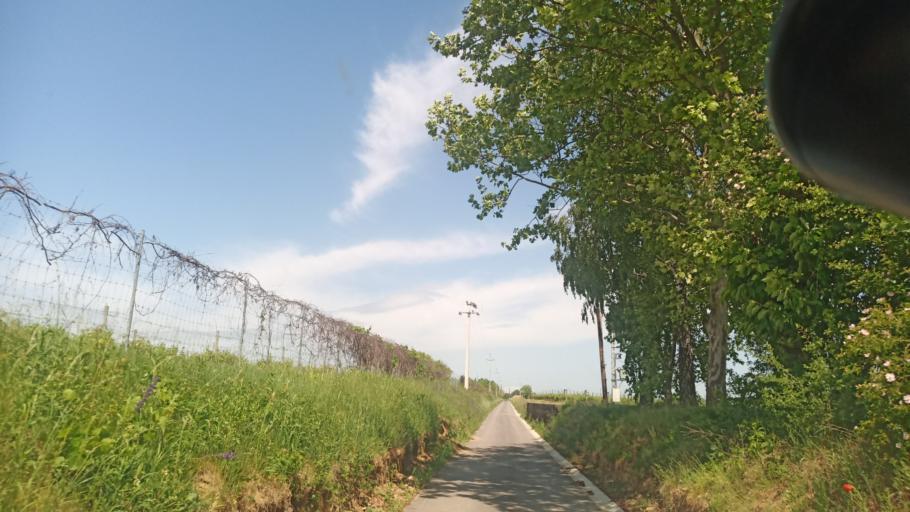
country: HU
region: Zala
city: Zalakomar
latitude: 46.6091
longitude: 17.1048
